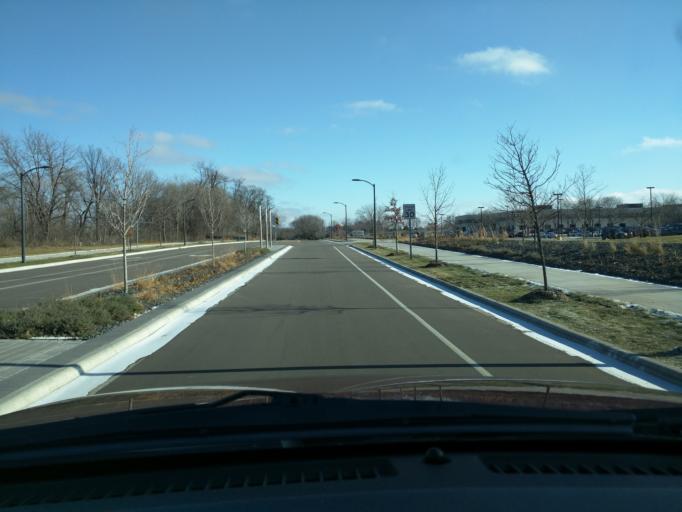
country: US
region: Minnesota
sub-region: Hennepin County
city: Eden Prairie
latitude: 44.8764
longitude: -93.4137
